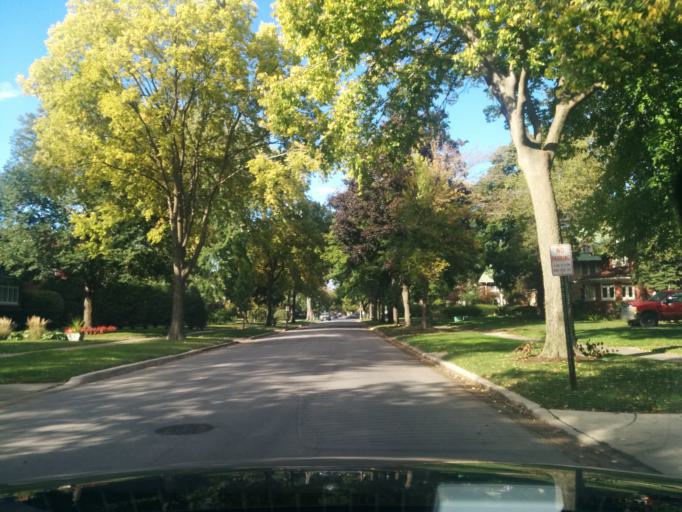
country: US
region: Illinois
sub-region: Cook County
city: River Forest
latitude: 41.8964
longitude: -87.8068
